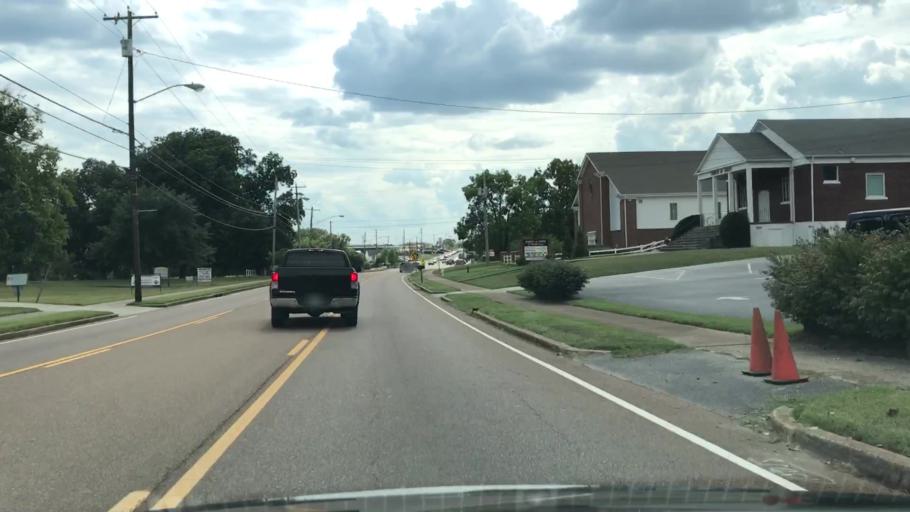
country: US
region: Tennessee
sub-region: Maury County
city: Spring Hill
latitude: 35.7494
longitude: -86.9321
